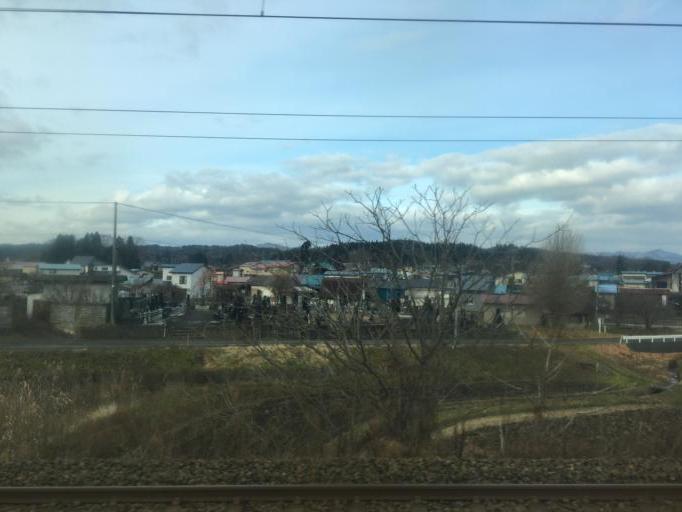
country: JP
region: Akita
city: Takanosu
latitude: 40.2540
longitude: 140.4015
